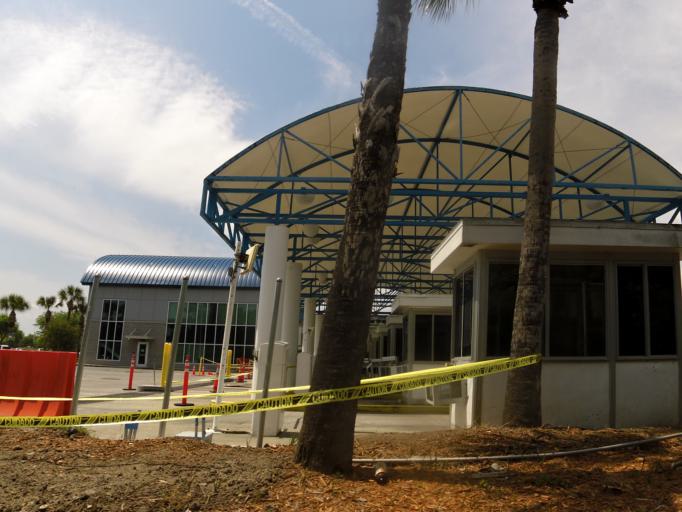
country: US
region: Florida
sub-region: Nassau County
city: Nassau Village-Ratliff
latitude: 30.4902
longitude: -81.6795
